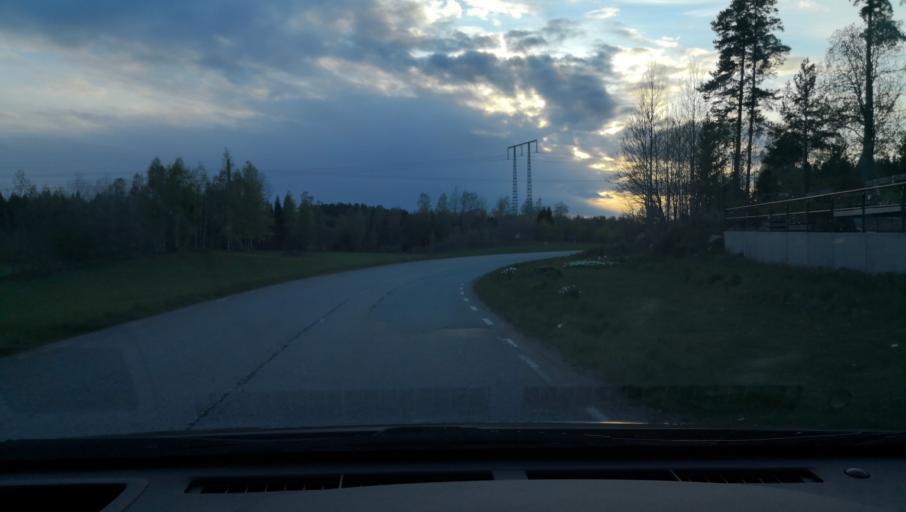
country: SE
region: OErebro
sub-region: Askersunds Kommun
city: Asbro
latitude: 58.9354
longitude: 15.0193
